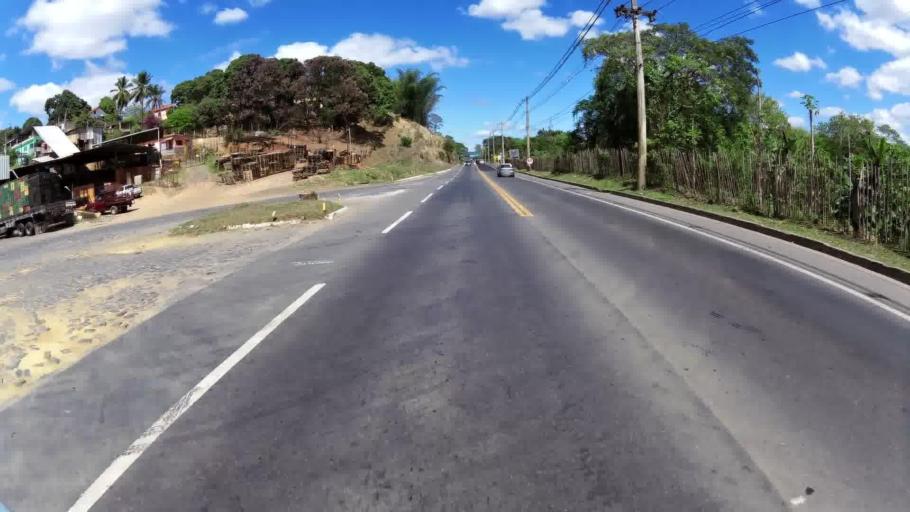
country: BR
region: Minas Gerais
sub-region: Alem Paraiba
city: Alem Paraiba
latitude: -21.8783
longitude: -42.6771
